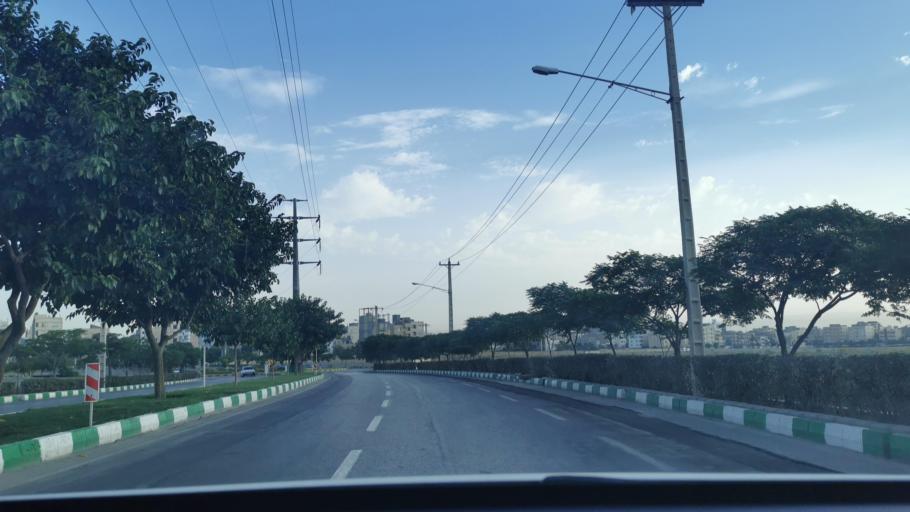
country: IR
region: Razavi Khorasan
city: Mashhad
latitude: 36.3486
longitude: 59.5314
